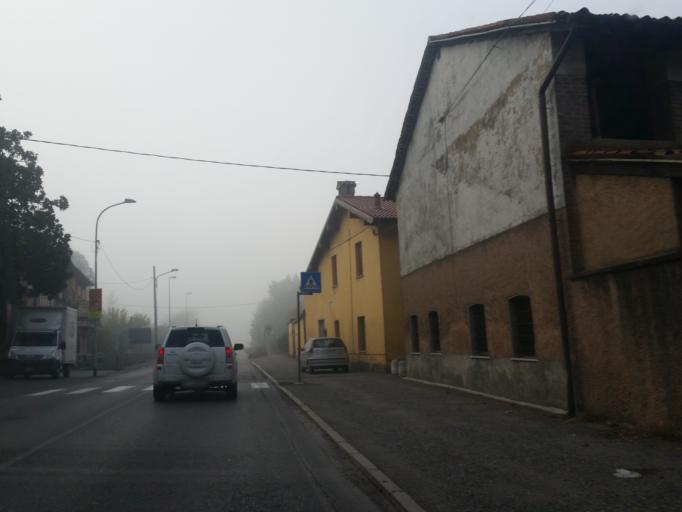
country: IT
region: Lombardy
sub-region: Provincia di Brescia
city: Dello
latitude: 45.4173
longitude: 10.0803
